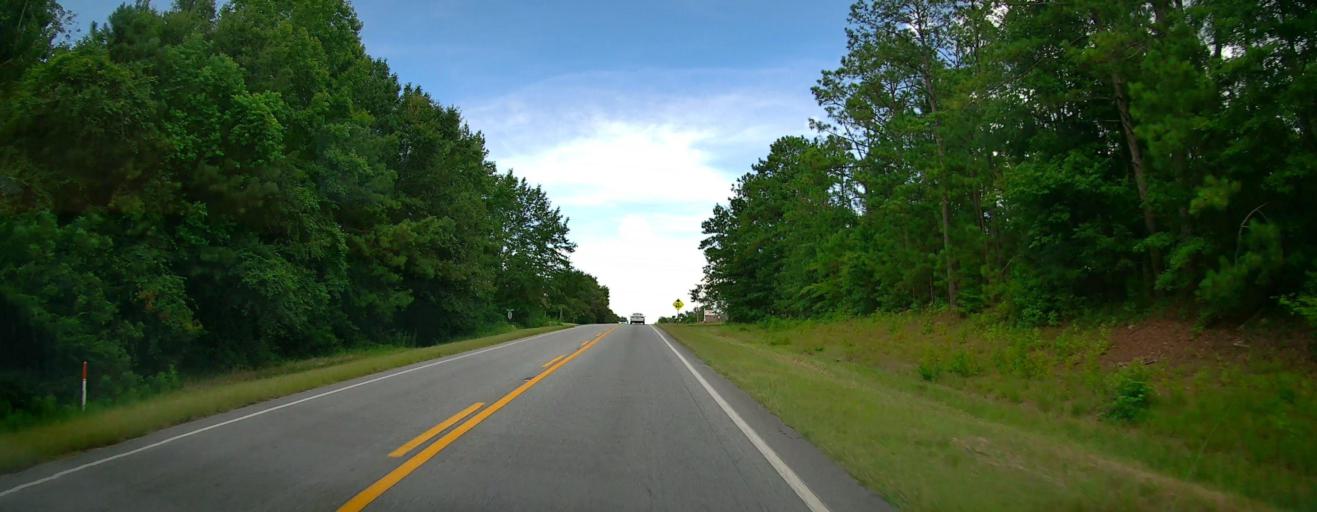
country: US
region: Alabama
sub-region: Russell County
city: Ladonia
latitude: 32.4532
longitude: -85.2082
